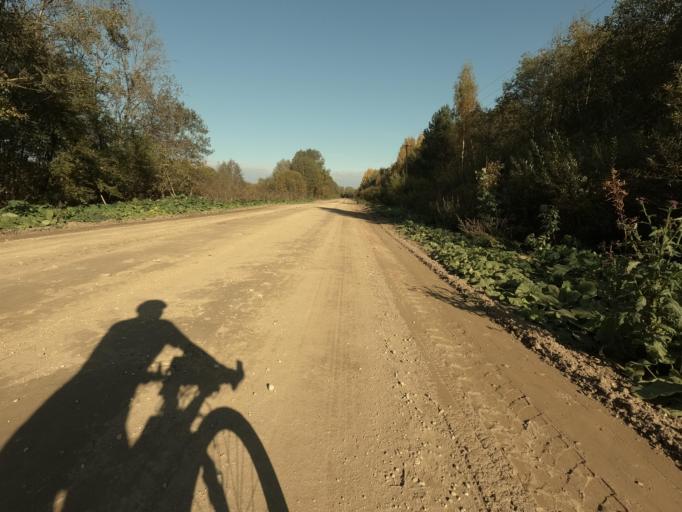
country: RU
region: Novgorod
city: Batetskiy
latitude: 58.8763
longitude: 30.7259
